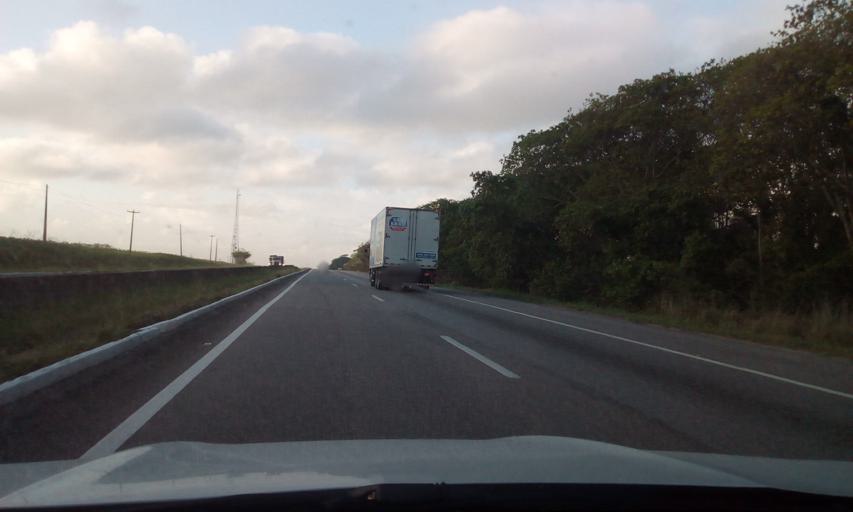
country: BR
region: Paraiba
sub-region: Alhandra
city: Alhandra
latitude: -7.4457
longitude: -34.9789
